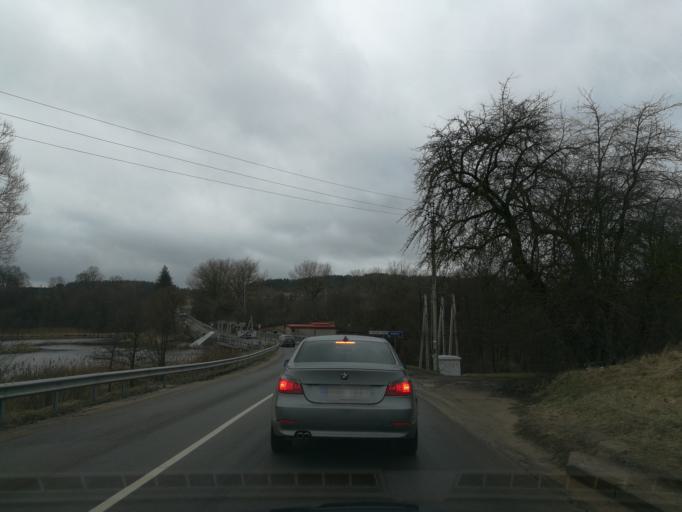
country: LT
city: Grigiskes
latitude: 54.6479
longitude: 25.1212
